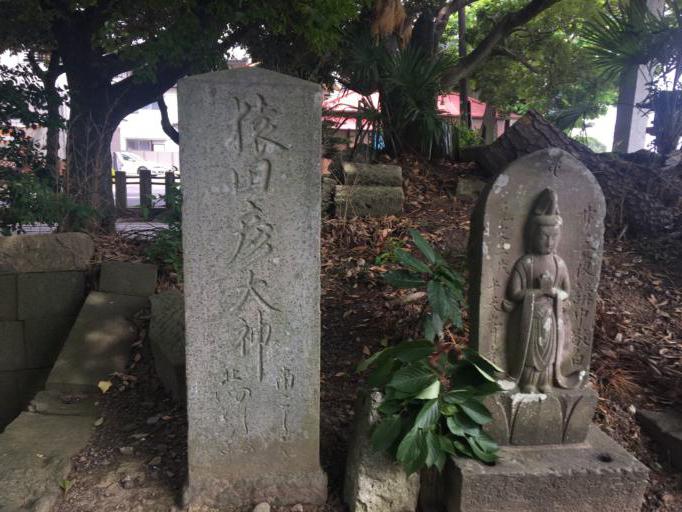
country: JP
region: Saitama
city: Koshigaya
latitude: 35.8976
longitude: 139.7893
